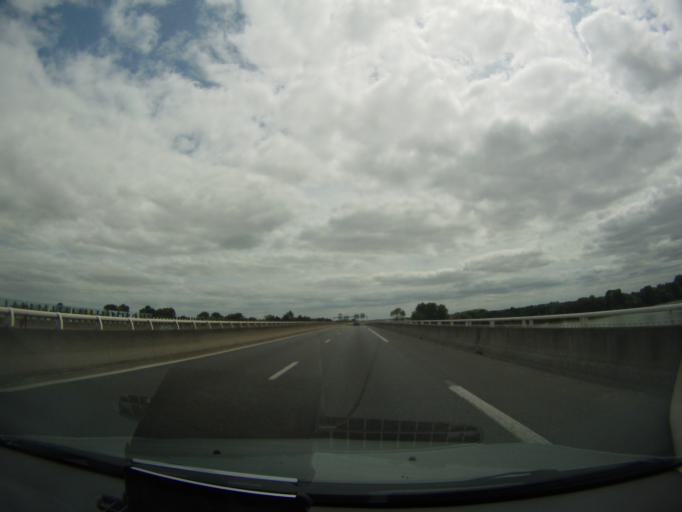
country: FR
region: Pays de la Loire
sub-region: Departement de la Loire-Atlantique
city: Basse-Goulaine
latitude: 47.2325
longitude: -1.4736
